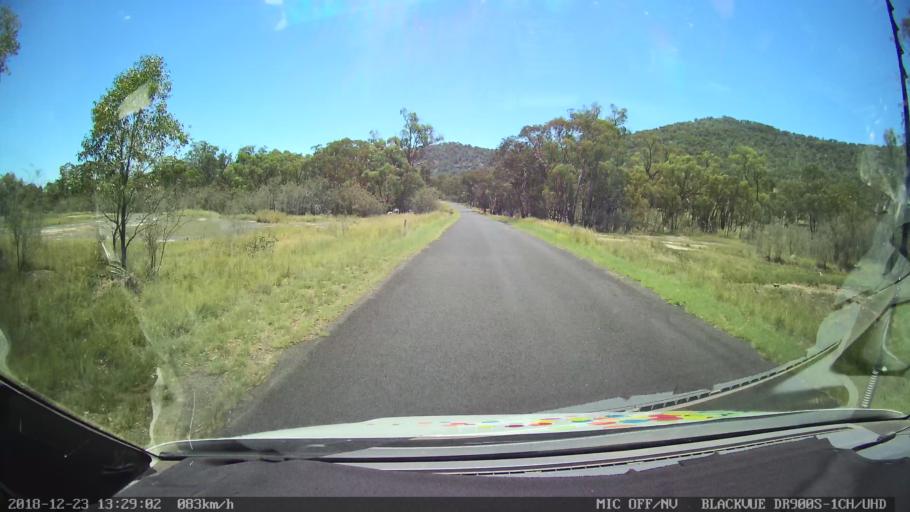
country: AU
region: New South Wales
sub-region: Armidale Dumaresq
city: Armidale
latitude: -30.4651
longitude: 151.3409
